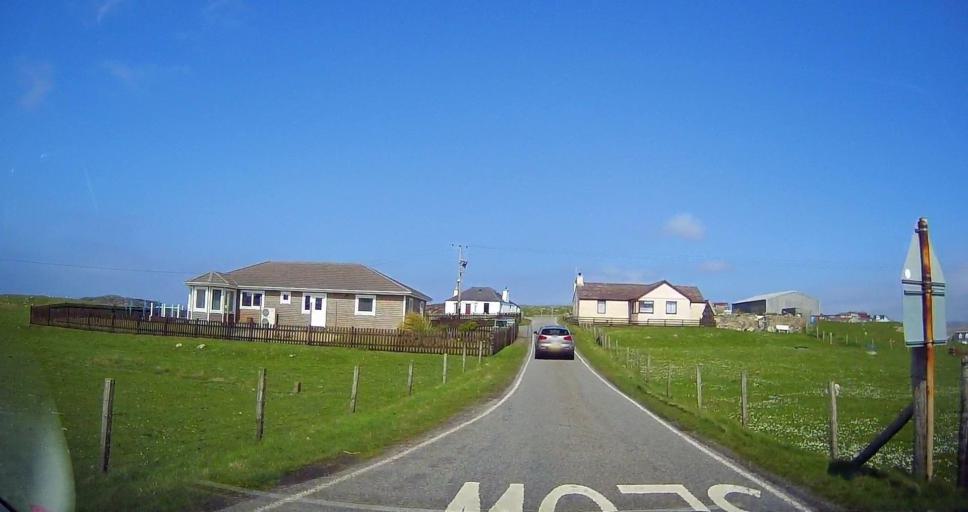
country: GB
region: Scotland
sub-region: Shetland Islands
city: Sandwick
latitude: 60.0831
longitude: -1.3321
